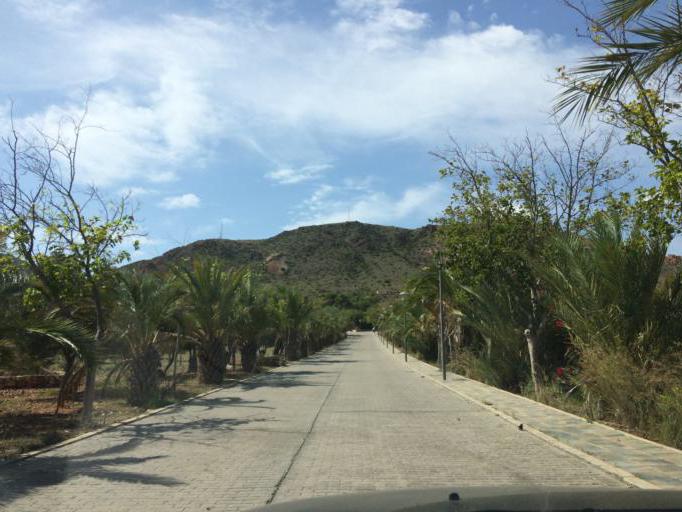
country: ES
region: Andalusia
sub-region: Provincia de Almeria
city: San Jose
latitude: 36.8488
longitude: -2.0413
